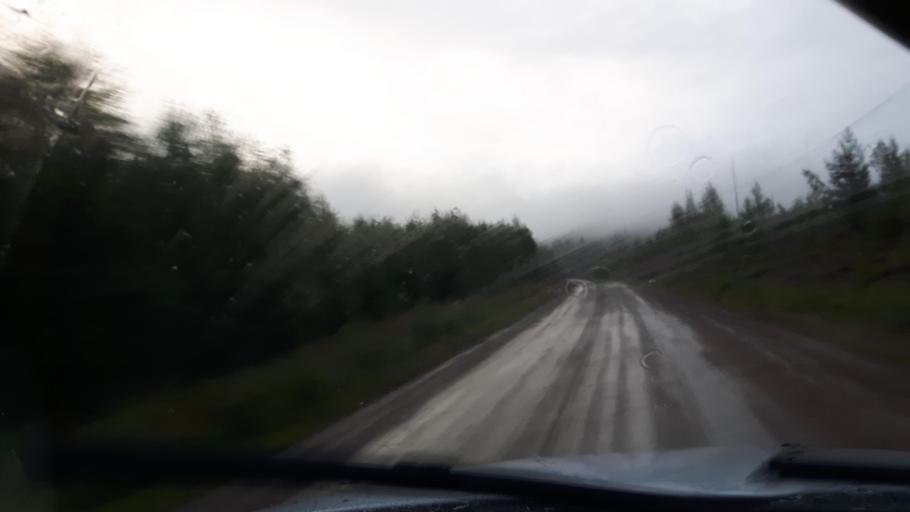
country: SE
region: Vaesternorrland
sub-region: Ange Kommun
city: Ange
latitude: 62.1712
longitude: 15.6444
